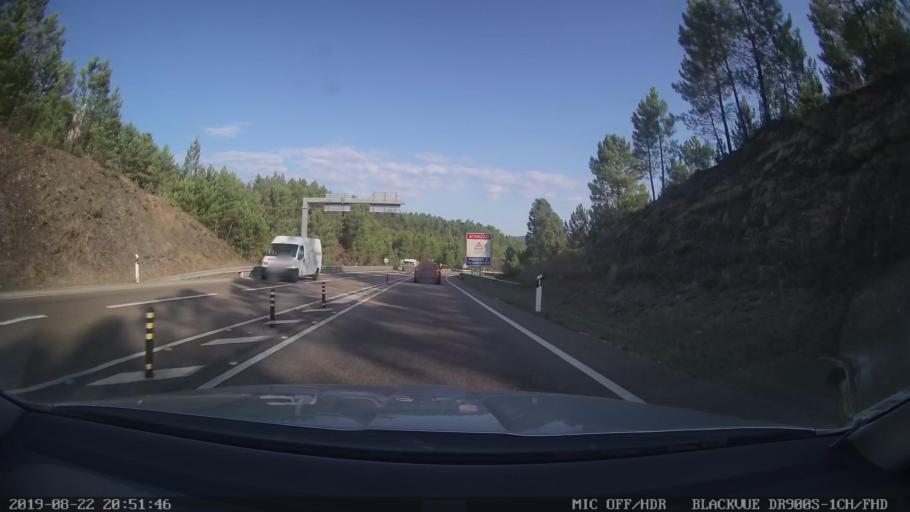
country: PT
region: Castelo Branco
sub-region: Proenca-A-Nova
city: Proenca-a-Nova
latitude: 39.7626
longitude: -7.9655
